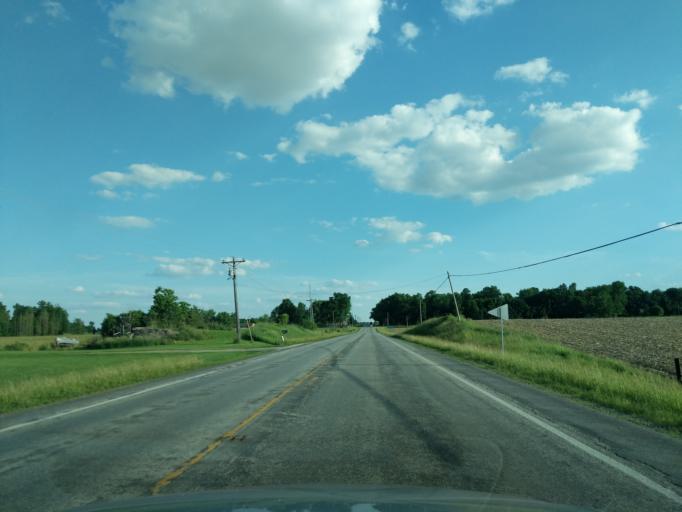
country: US
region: Indiana
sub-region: Whitley County
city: Columbia City
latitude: 41.1074
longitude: -85.4715
